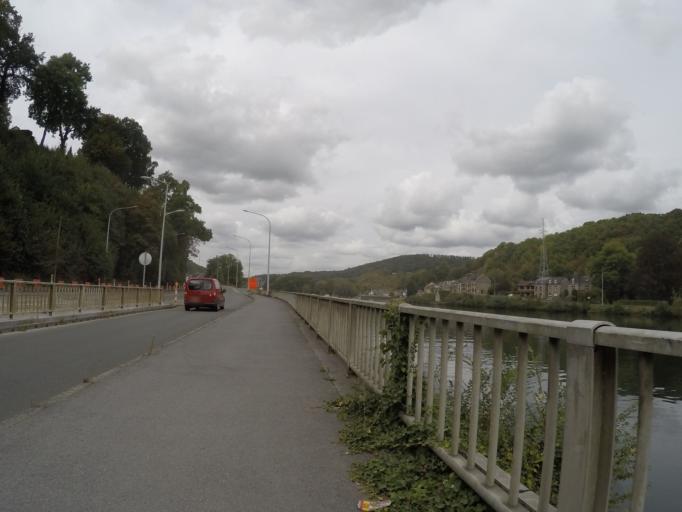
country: BE
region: Wallonia
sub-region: Province de Namur
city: Anhee
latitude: 50.3174
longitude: 4.8763
